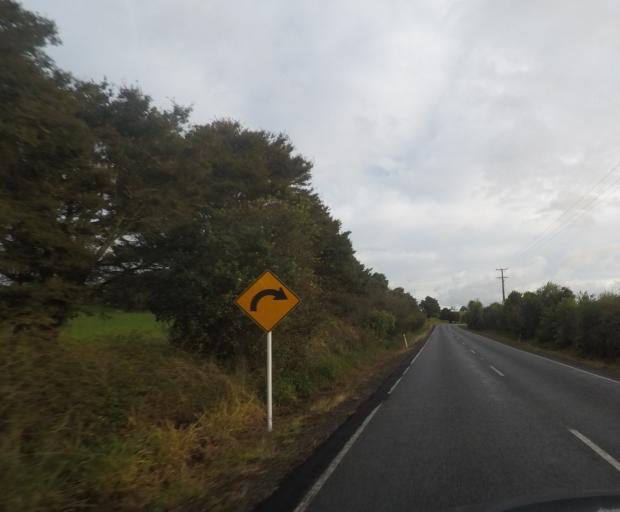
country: NZ
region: Auckland
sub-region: Auckland
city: Wellsford
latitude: -36.2125
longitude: 174.5854
